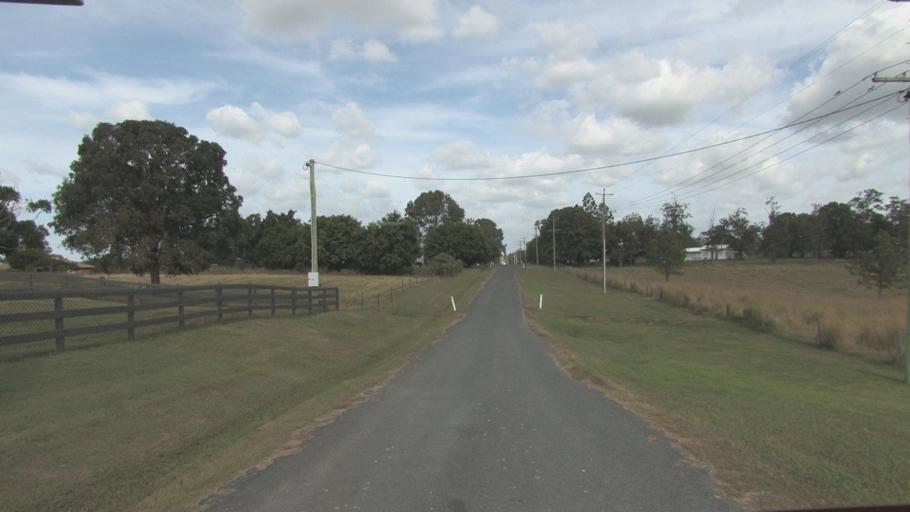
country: AU
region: Queensland
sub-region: Logan
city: Slacks Creek
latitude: -27.6762
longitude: 153.1596
